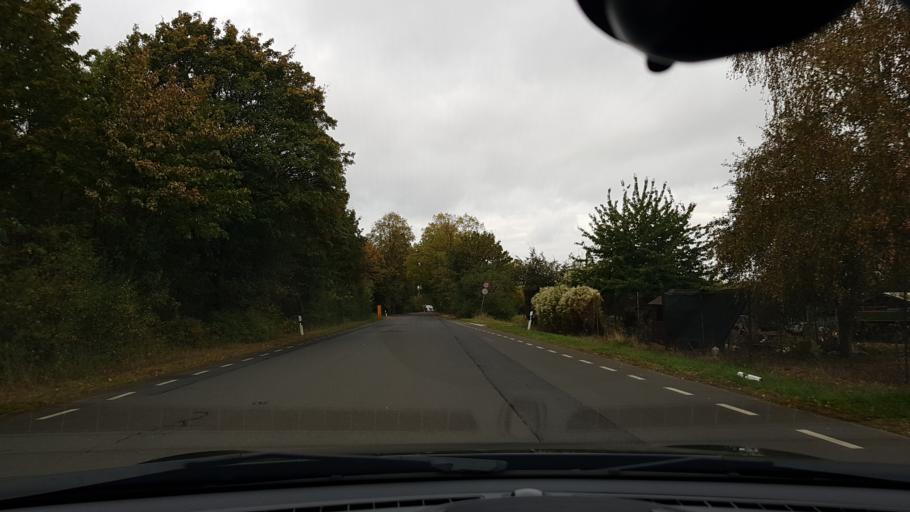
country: DE
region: North Rhine-Westphalia
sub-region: Regierungsbezirk Koln
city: Elsdorf
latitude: 50.9333
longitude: 6.5495
